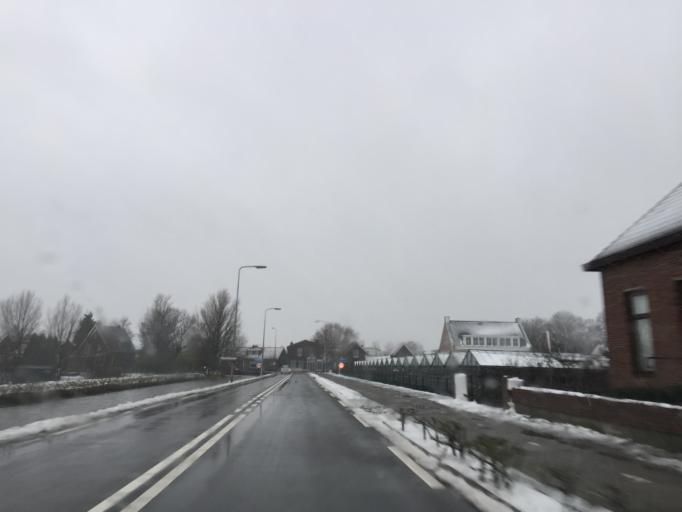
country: NL
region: South Holland
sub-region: Gemeente Pijnacker-Nootdorp
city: Pijnacker
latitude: 52.0293
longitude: 4.4358
